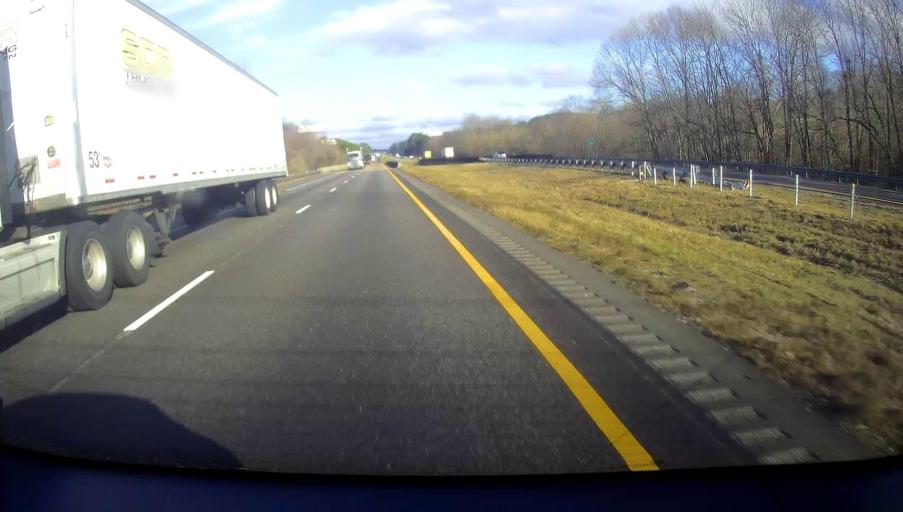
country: US
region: Alabama
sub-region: Cleburne County
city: Heflin
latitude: 33.6372
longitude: -85.5315
